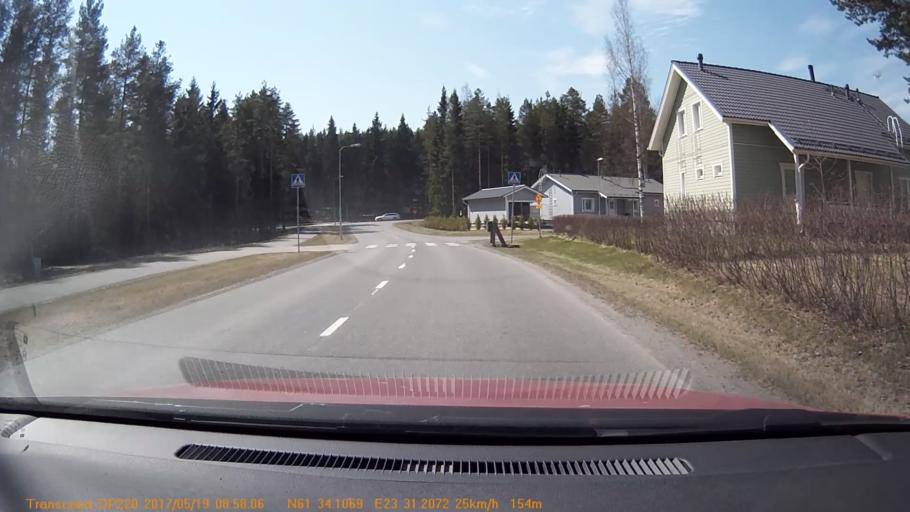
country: FI
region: Pirkanmaa
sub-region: Tampere
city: Yloejaervi
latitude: 61.5685
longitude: 23.5202
